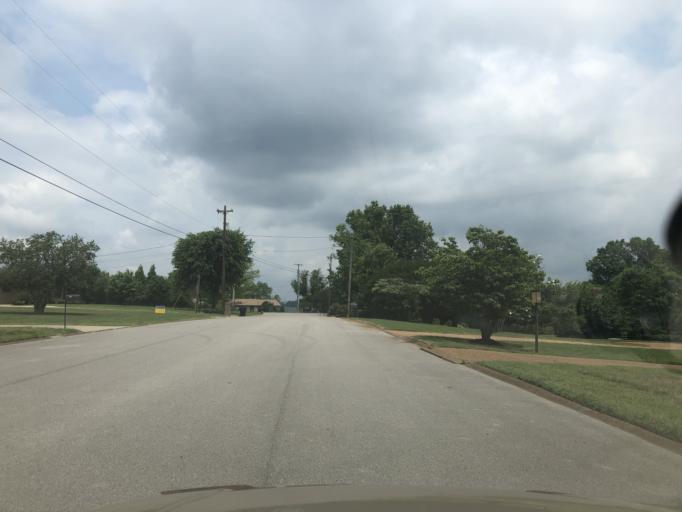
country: US
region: Tennessee
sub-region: Davidson County
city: Lakewood
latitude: 36.2421
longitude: -86.6220
